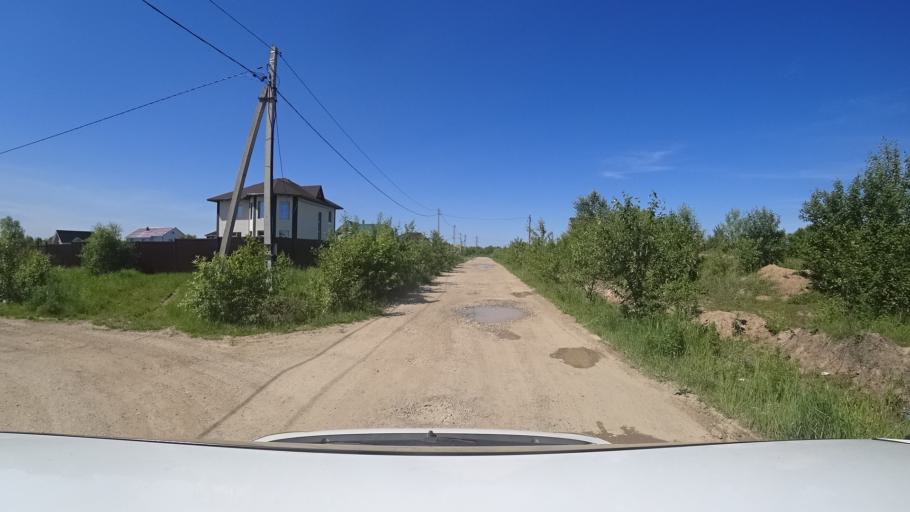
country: RU
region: Khabarovsk Krai
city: Topolevo
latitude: 48.5644
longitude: 135.1926
